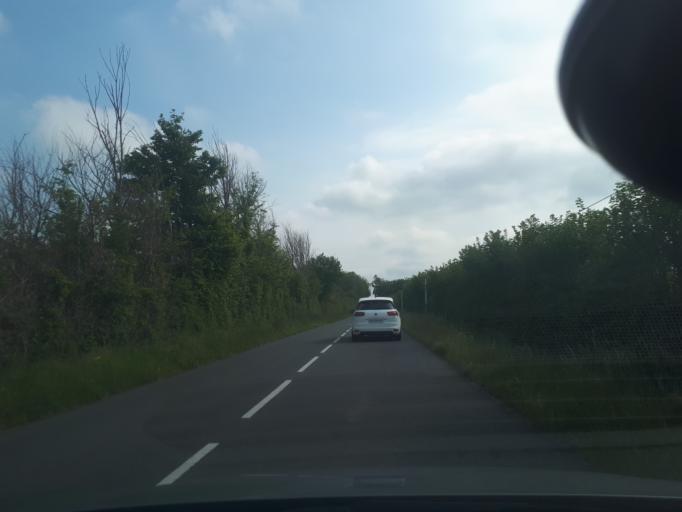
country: FR
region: Auvergne
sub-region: Departement de l'Allier
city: Dompierre-sur-Besbre
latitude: 46.4105
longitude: 3.6057
